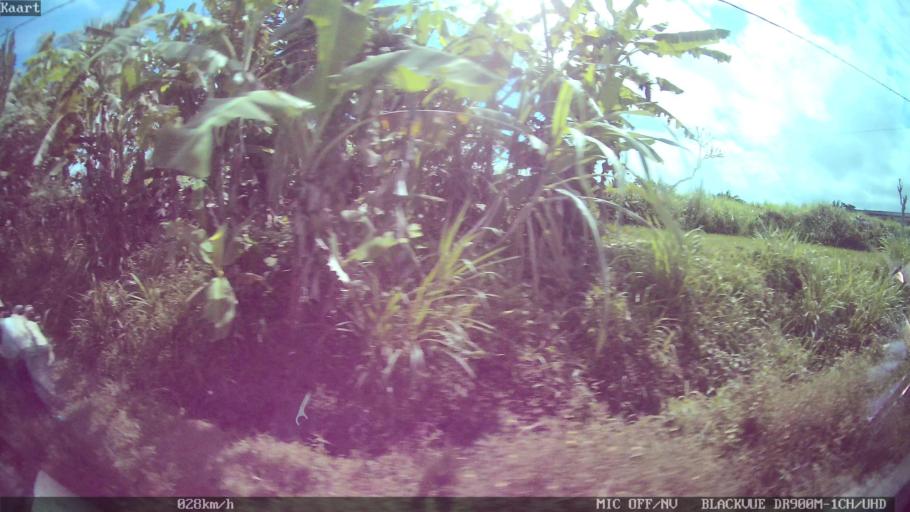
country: ID
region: Bali
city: Banjar Apuan Kaja
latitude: -8.4879
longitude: 115.3425
